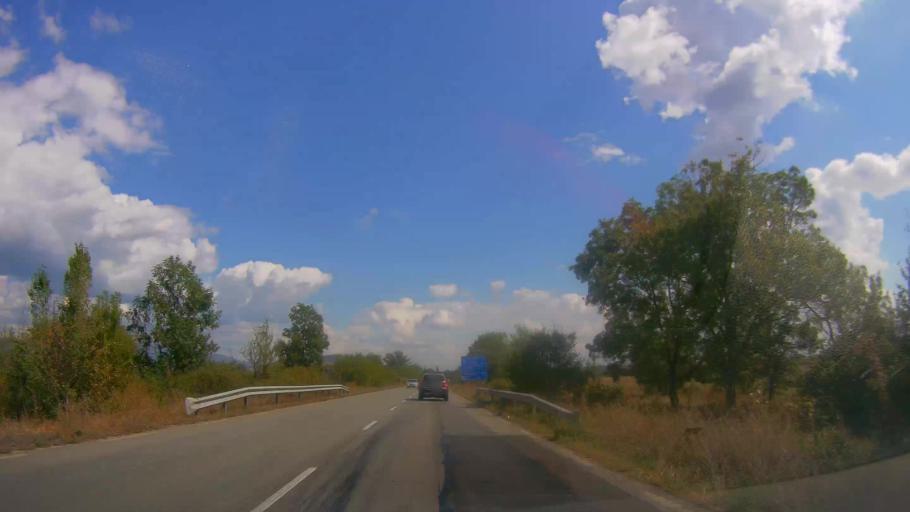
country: BG
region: Sliven
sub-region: Obshtina Tvurditsa
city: Tvurditsa
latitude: 42.6530
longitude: 25.9660
